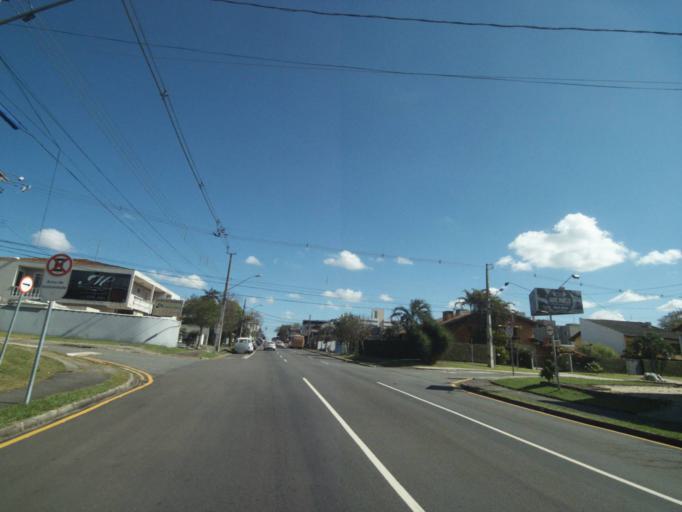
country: BR
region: Parana
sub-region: Curitiba
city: Curitiba
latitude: -25.3982
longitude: -49.2586
